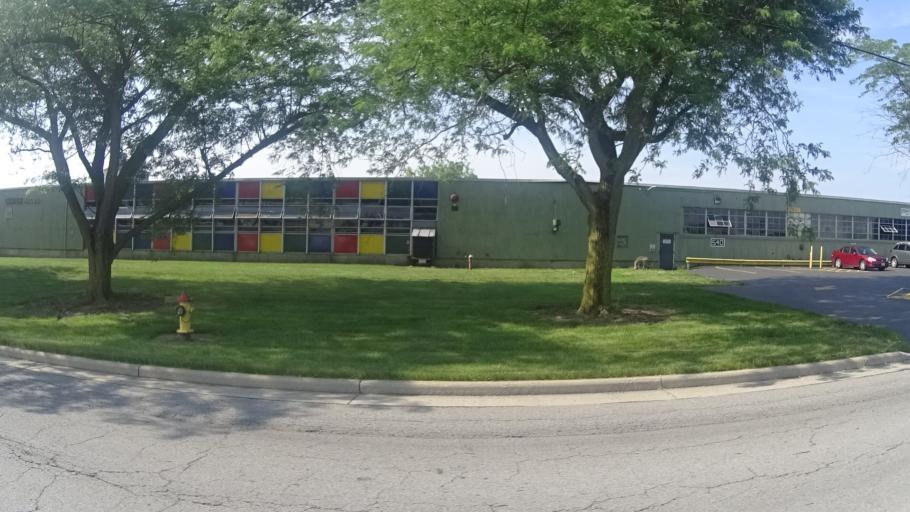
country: US
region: Ohio
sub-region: Huron County
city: Bellevue
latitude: 41.2837
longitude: -82.8321
